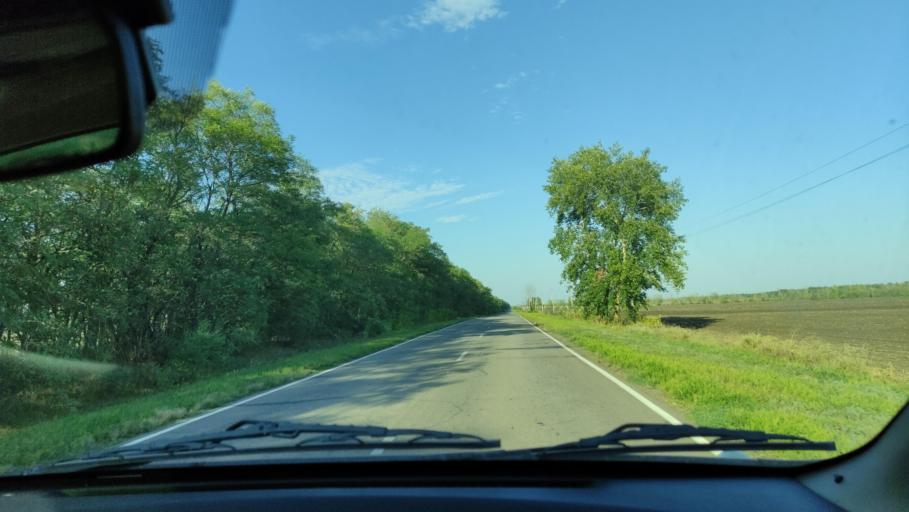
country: RU
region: Voronezj
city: Verkhniy Mamon
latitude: 50.1259
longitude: 40.3147
